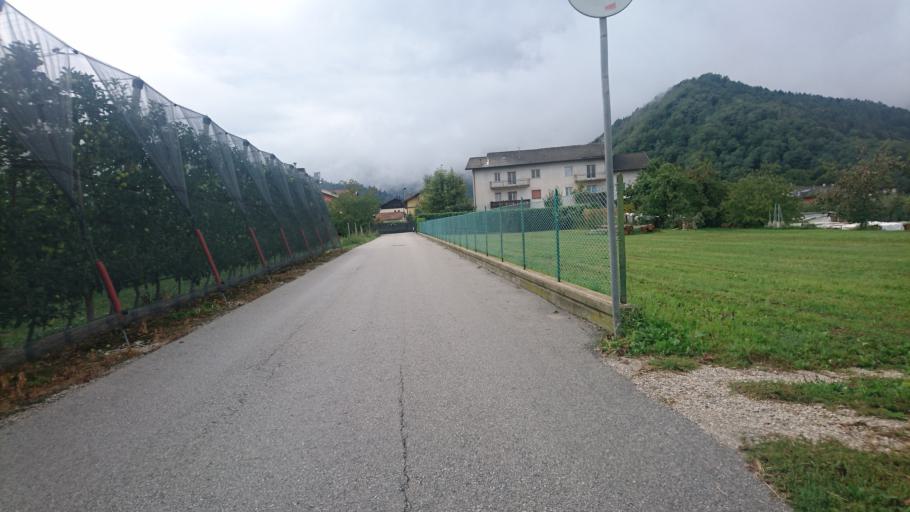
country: IT
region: Trentino-Alto Adige
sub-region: Provincia di Trento
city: Caldonazzo
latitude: 45.9887
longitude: 11.2694
